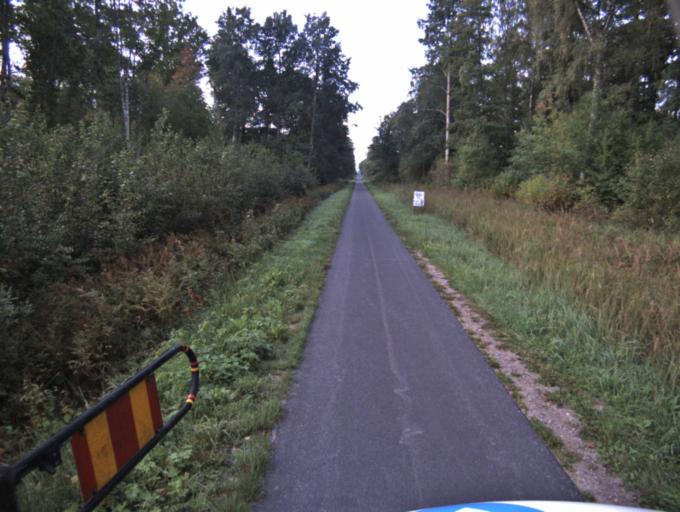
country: SE
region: Vaestra Goetaland
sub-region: Ulricehamns Kommun
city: Ulricehamn
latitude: 57.7188
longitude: 13.3987
